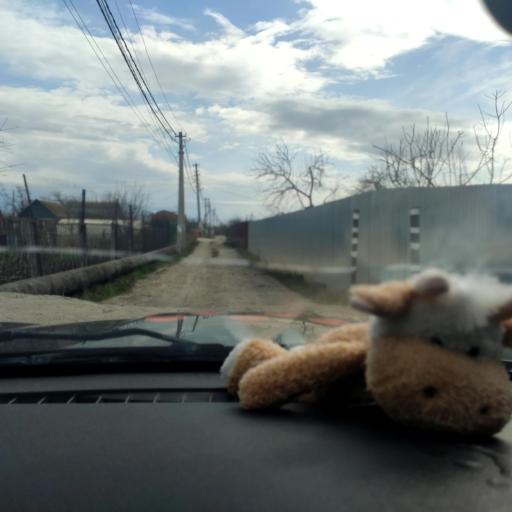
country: RU
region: Samara
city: Podstepki
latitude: 53.5947
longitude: 49.2250
